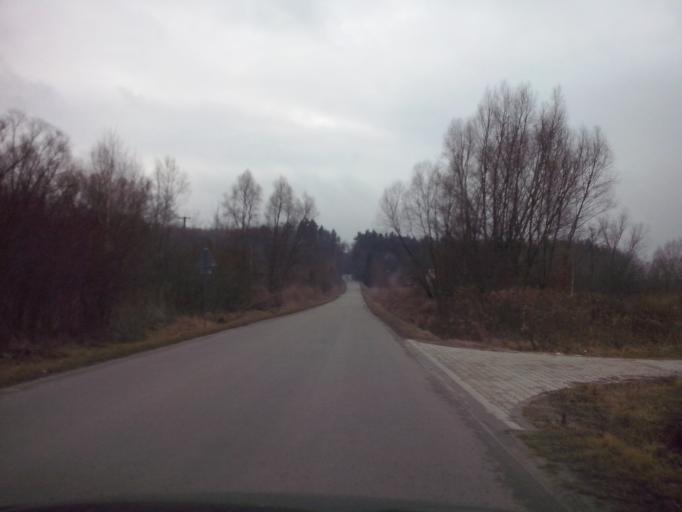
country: PL
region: Subcarpathian Voivodeship
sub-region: Powiat nizanski
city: Bieliny
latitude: 50.4381
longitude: 22.3039
